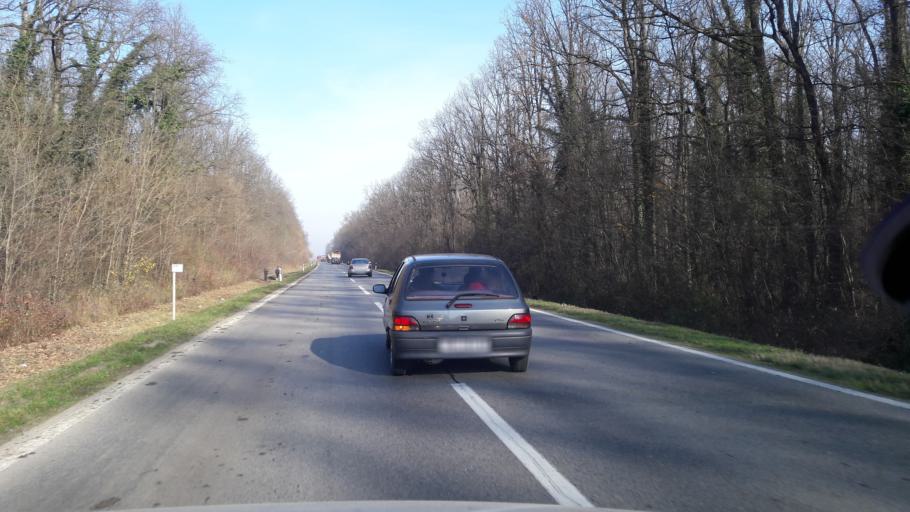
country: HR
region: Vukovarsko-Srijemska
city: Gradiste
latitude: 45.1259
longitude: 18.7141
